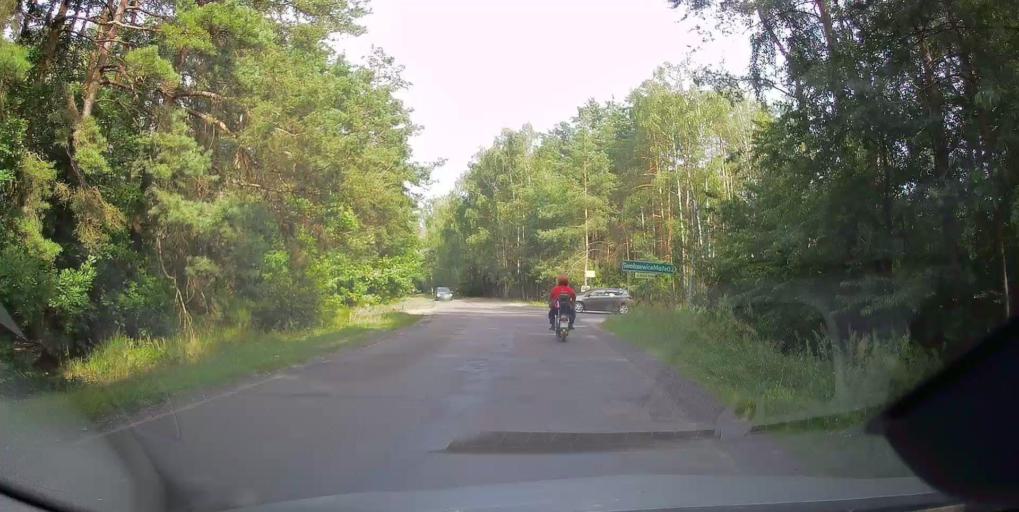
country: PL
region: Lodz Voivodeship
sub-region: Powiat tomaszowski
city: Tomaszow Mazowiecki
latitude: 51.4743
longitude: 19.9893
